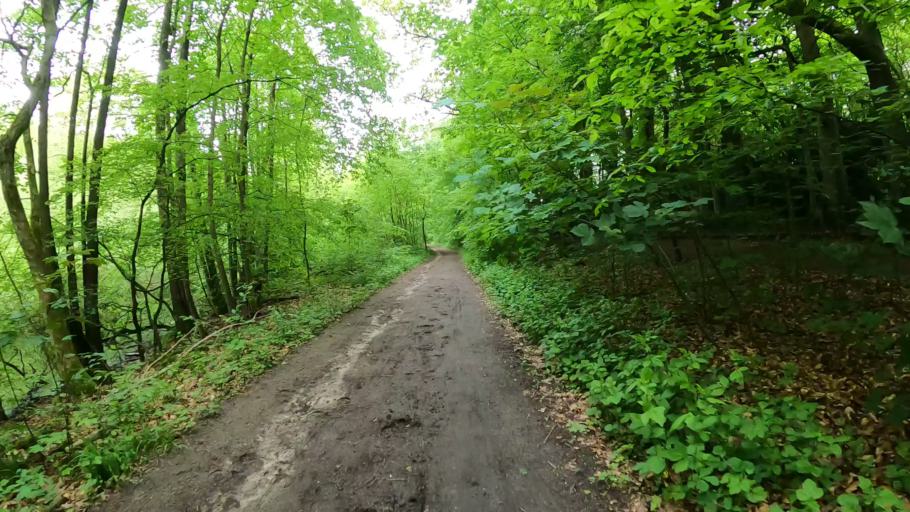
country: DE
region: Hamburg
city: Wohldorf-Ohlstedt
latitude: 53.6897
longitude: 10.1225
